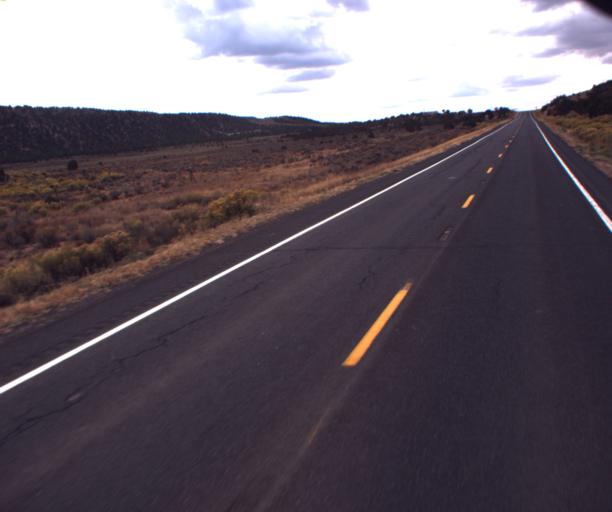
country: US
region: Arizona
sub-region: Navajo County
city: Kayenta
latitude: 36.5656
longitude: -110.4922
